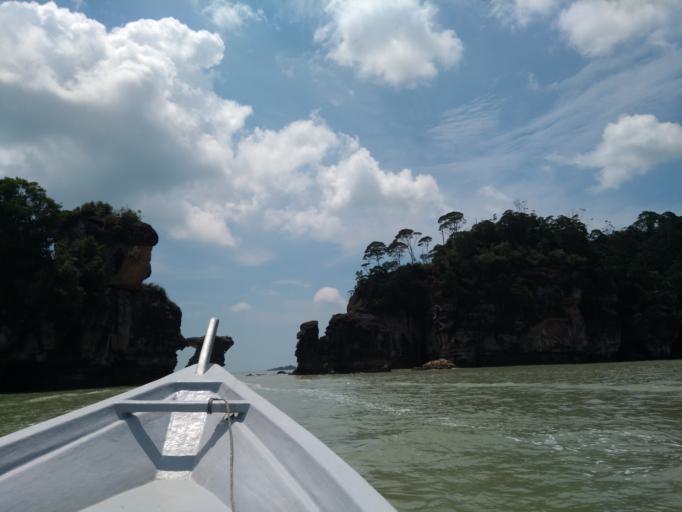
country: MY
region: Sarawak
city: Kuching
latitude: 1.7312
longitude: 110.4465
